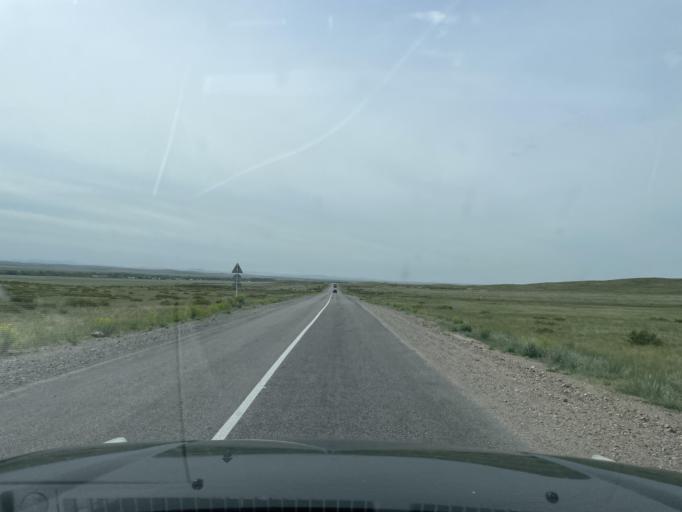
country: KZ
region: Qaraghandy
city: Abay
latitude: 49.4489
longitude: 72.9217
